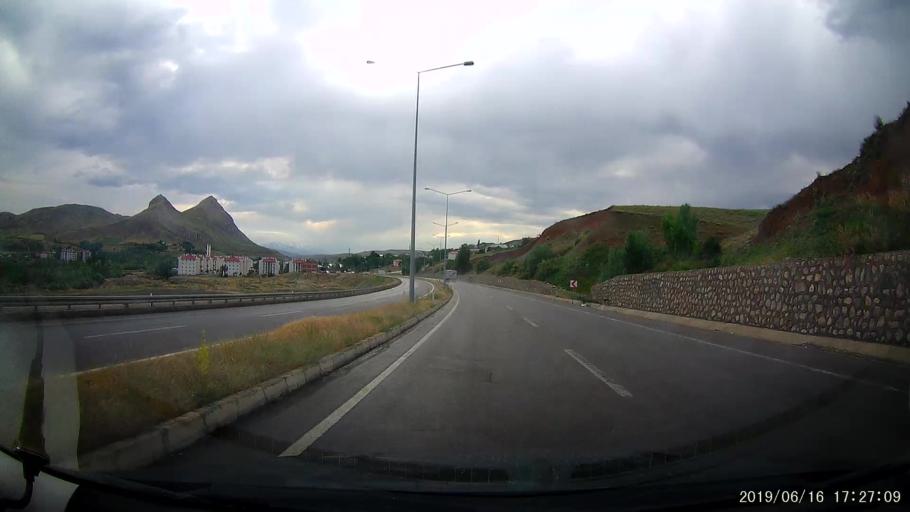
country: TR
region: Erzincan
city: Tercan
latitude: 39.7752
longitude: 40.3984
